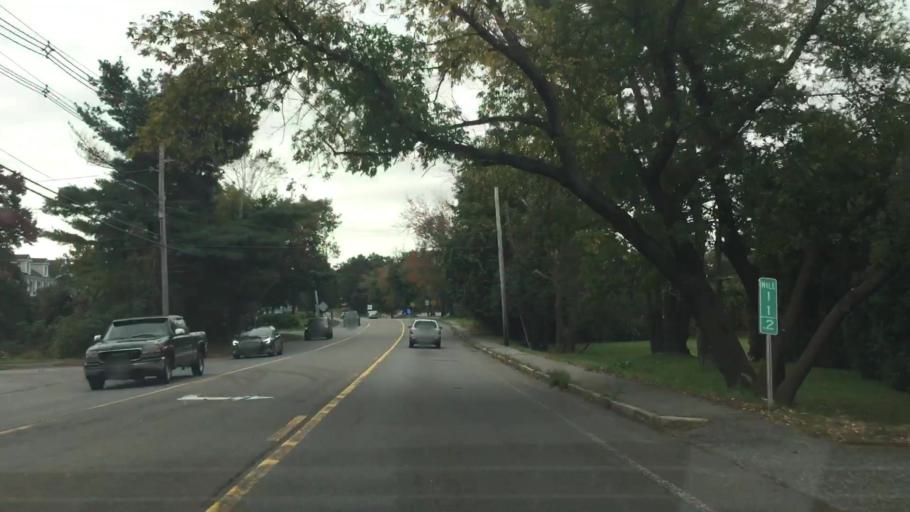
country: US
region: Massachusetts
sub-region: Essex County
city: Middleton
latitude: 42.5895
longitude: -71.0124
